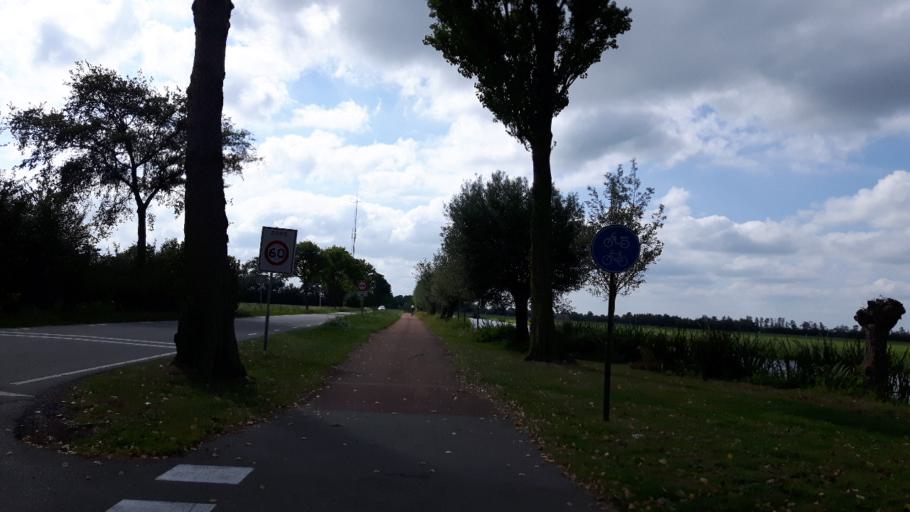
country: NL
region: Utrecht
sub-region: Gemeente Woerden
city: Woerden
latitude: 52.1243
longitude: 4.8500
